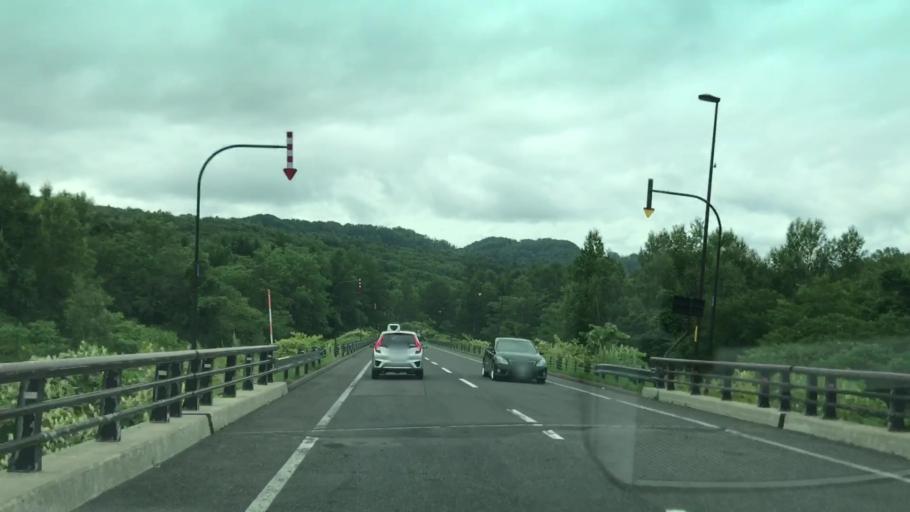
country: JP
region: Hokkaido
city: Niseko Town
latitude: 42.9508
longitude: 140.8537
